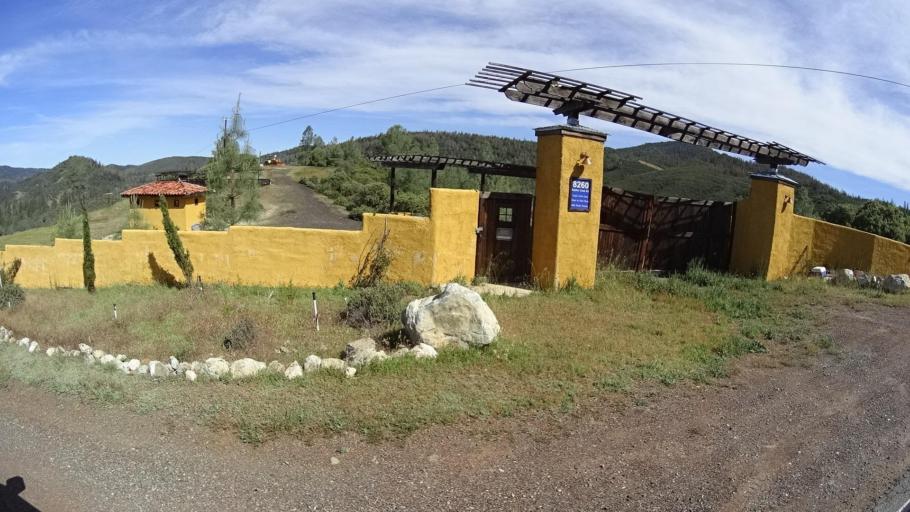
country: US
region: California
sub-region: Lake County
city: Cobb
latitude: 38.8569
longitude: -122.7519
